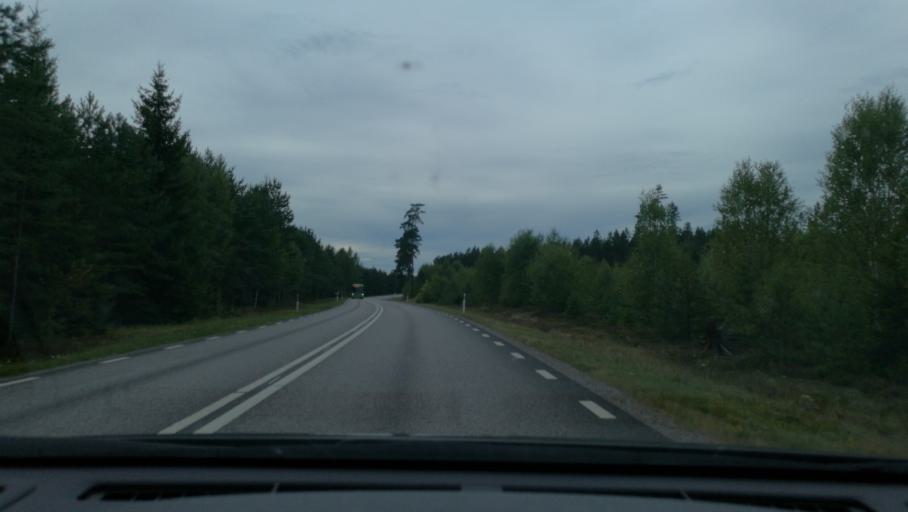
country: SE
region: Soedermanland
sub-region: Katrineholms Kommun
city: Katrineholm
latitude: 59.1175
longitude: 16.1620
